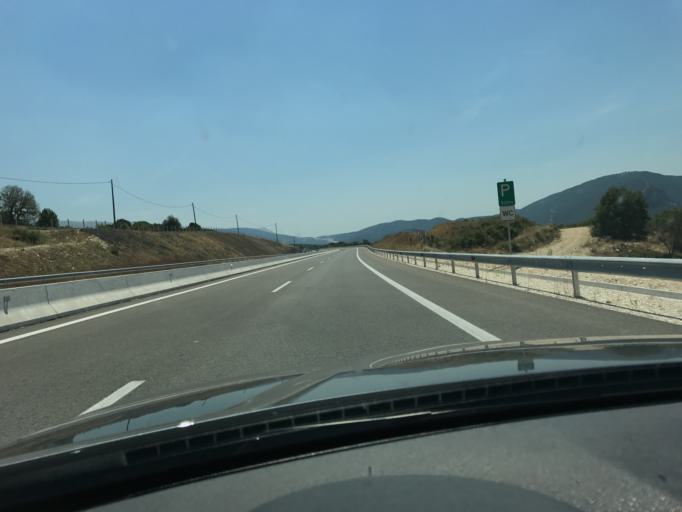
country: GR
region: Epirus
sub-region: Nomos Ioanninon
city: Agia Kyriaki
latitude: 39.4773
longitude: 20.8948
